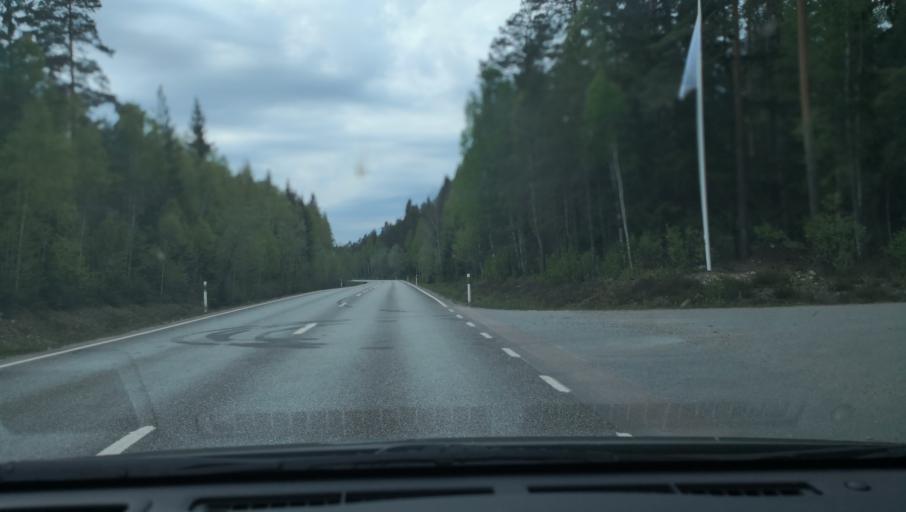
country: SE
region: Vaestmanland
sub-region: Skinnskattebergs Kommun
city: Skinnskatteberg
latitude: 59.8032
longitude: 15.7339
